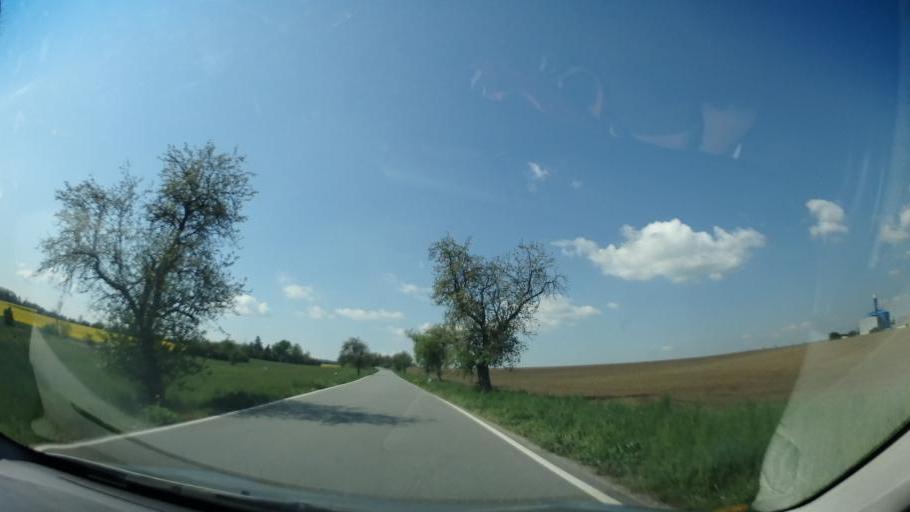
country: CZ
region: Vysocina
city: Namest' nad Oslavou
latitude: 49.2025
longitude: 16.0980
